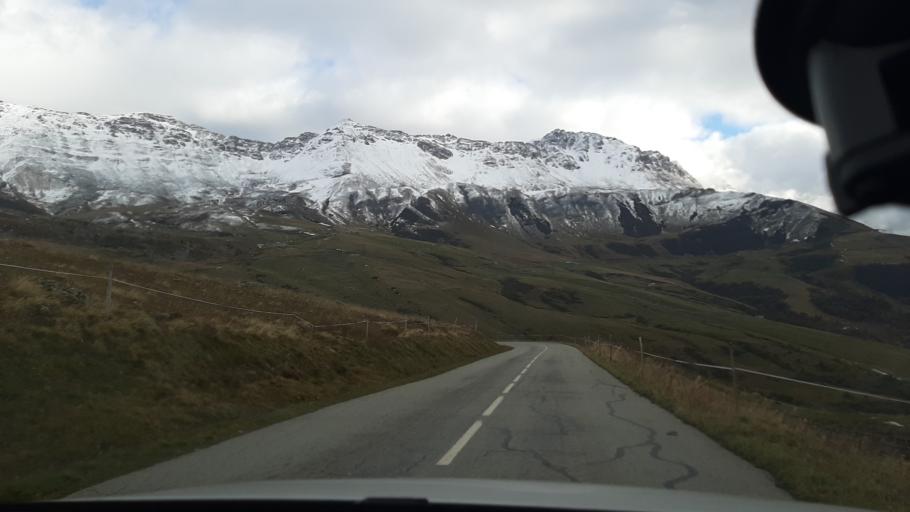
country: FR
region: Rhone-Alpes
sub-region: Departement de la Savoie
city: La Chambre
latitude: 45.4283
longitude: 6.3675
